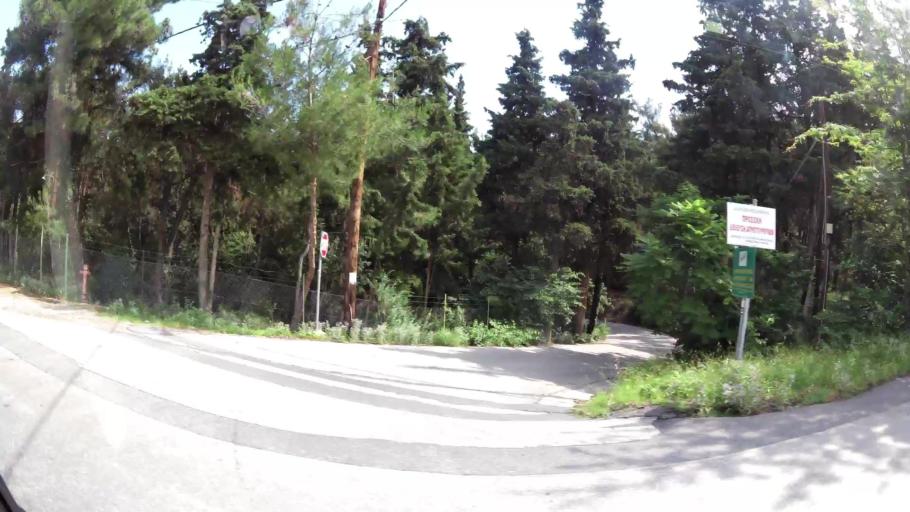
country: GR
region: Central Macedonia
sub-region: Nomos Thessalonikis
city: Panorama
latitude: 40.5919
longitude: 23.0174
